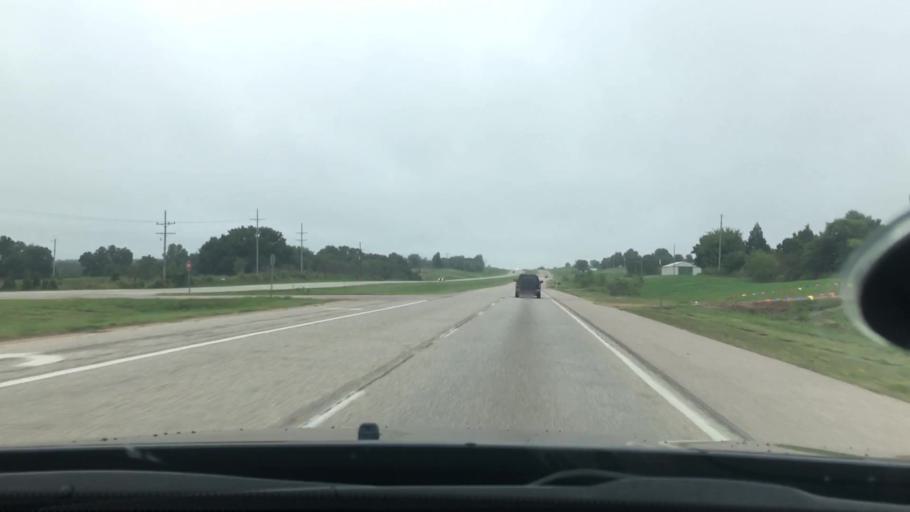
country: US
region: Oklahoma
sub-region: Seminole County
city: Seminole
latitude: 35.2967
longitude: -96.6708
